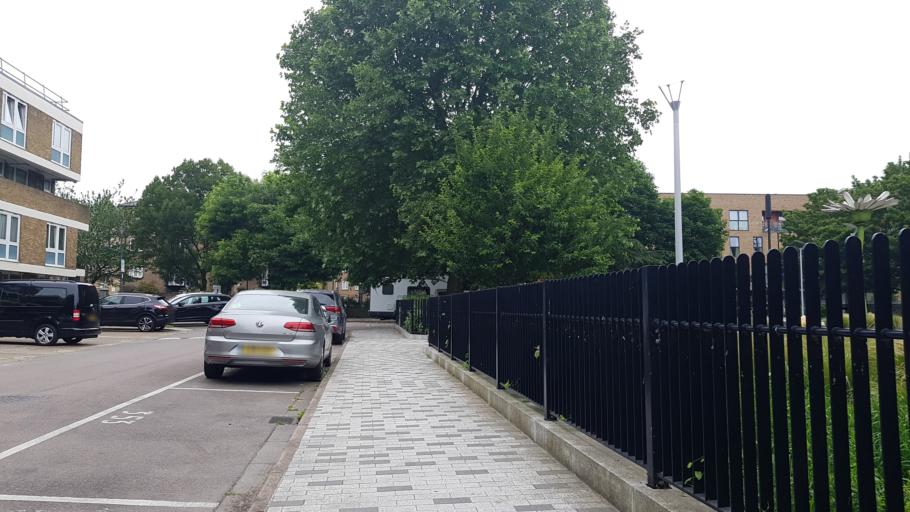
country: GB
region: England
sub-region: Greater London
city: Hackney
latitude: 51.5342
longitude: -0.0342
